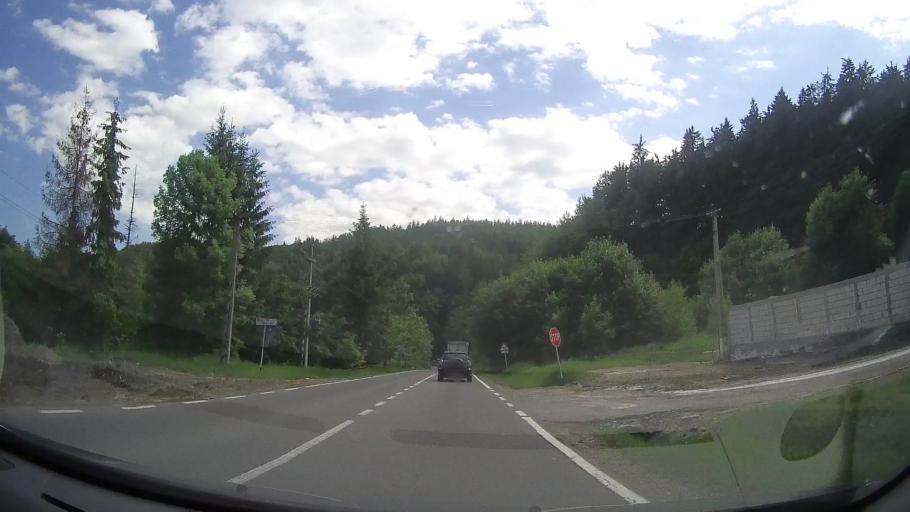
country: RO
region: Prahova
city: Maneciu
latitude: 45.3663
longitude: 25.9309
